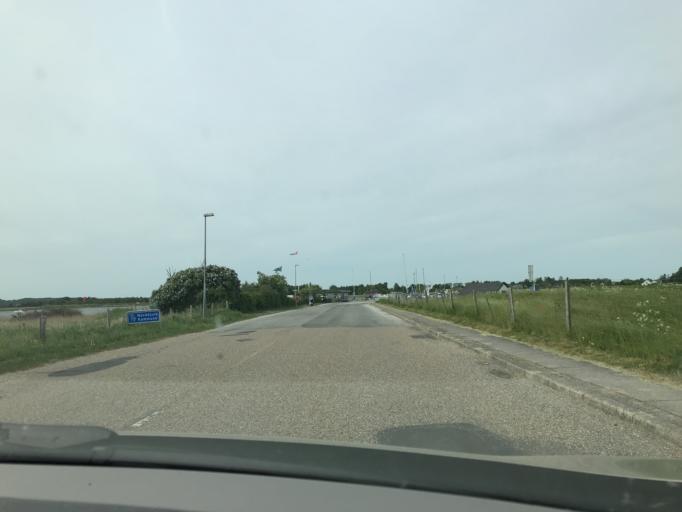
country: DK
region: Central Jutland
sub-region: Norddjurs Kommune
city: Allingabro
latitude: 56.6052
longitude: 10.3036
